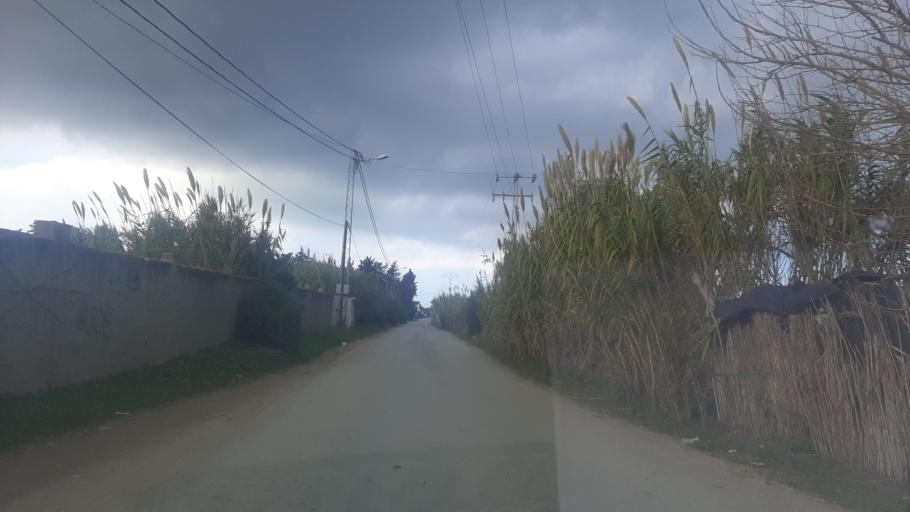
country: TN
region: Nabul
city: Manzil Bu Zalafah
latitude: 36.7307
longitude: 10.5393
